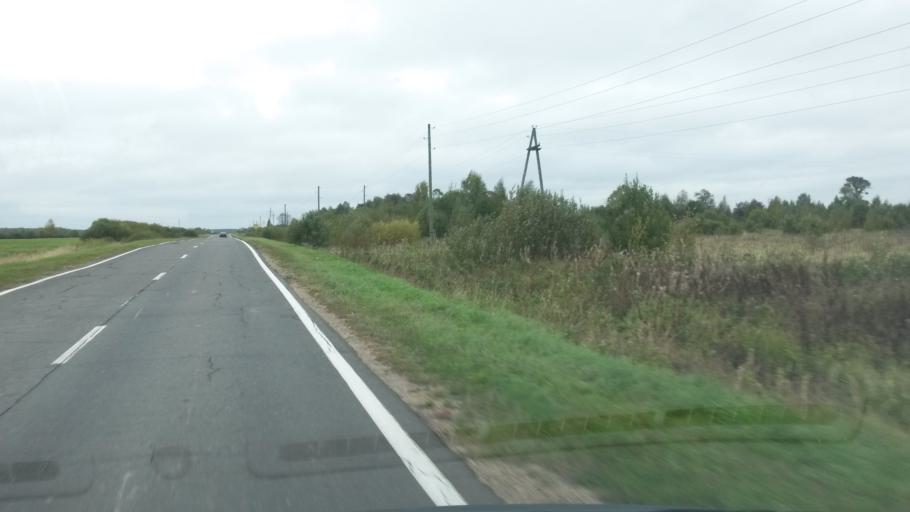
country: RU
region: Jaroslavl
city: Tutayev
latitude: 57.9504
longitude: 39.4400
